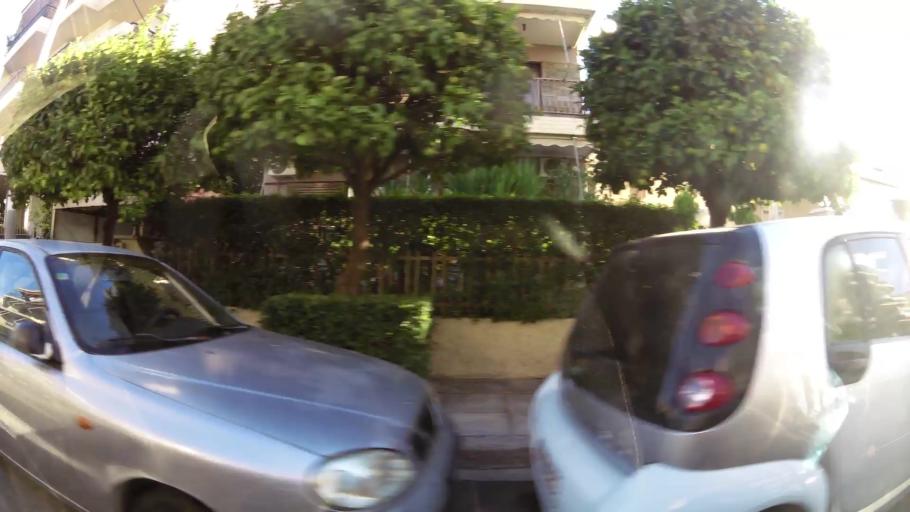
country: GR
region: Attica
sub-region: Nomarchia Athinas
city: Argyroupoli
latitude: 37.8889
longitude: 23.7556
